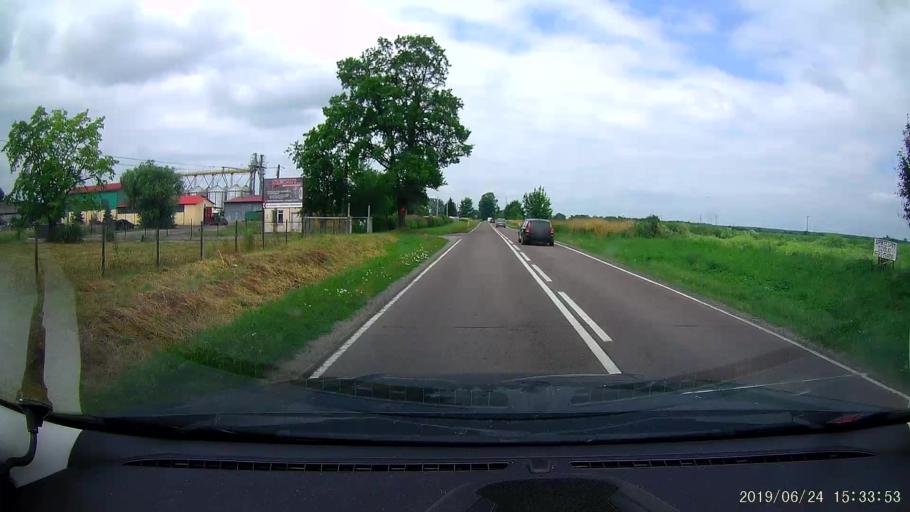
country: PL
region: Subcarpathian Voivodeship
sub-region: Powiat jaroslawski
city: Wiazownica
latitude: 50.0509
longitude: 22.7740
